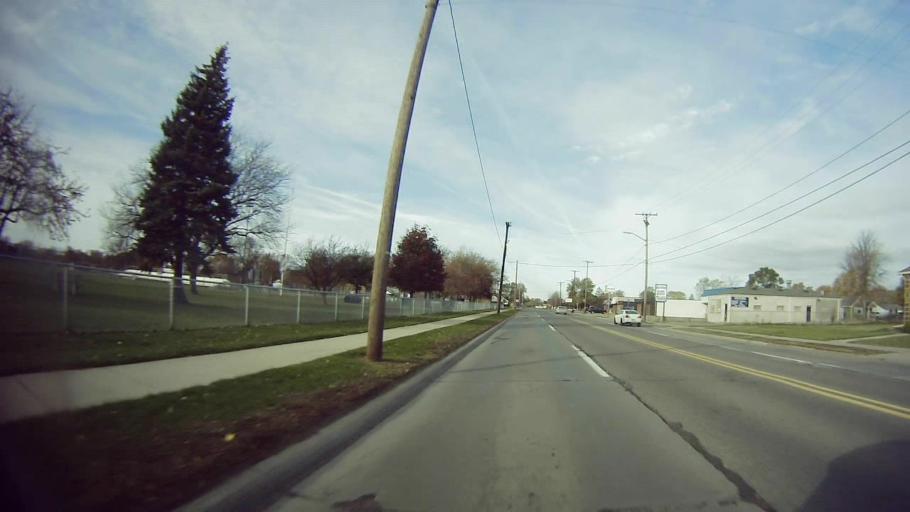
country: US
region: Michigan
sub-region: Macomb County
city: Eastpointe
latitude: 42.4795
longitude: -82.9624
